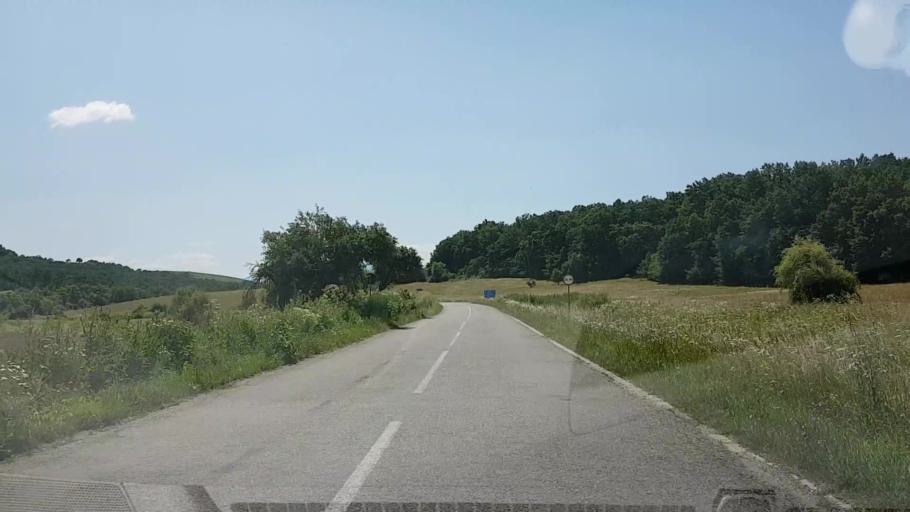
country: RO
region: Brasov
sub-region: Comuna Cincu
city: Cincu
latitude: 45.8721
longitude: 24.8206
